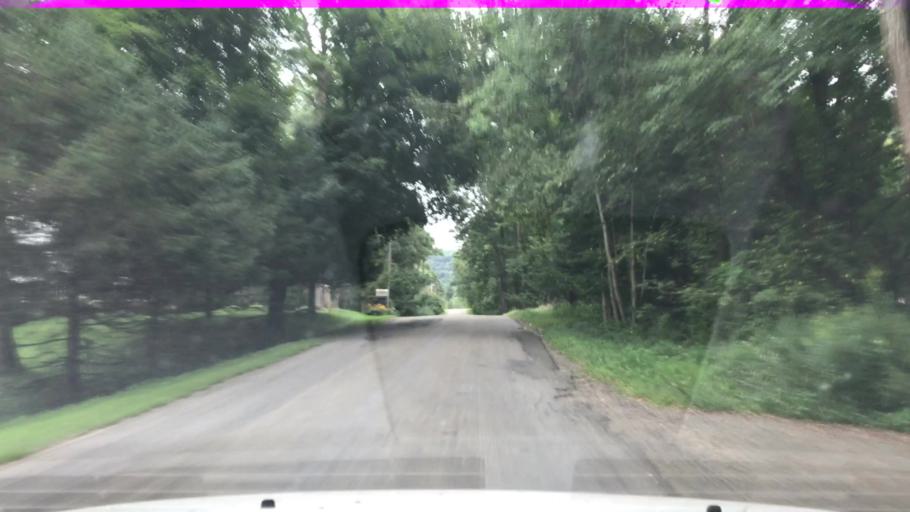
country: US
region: New York
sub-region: Cattaraugus County
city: Little Valley
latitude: 42.3117
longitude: -78.7191
